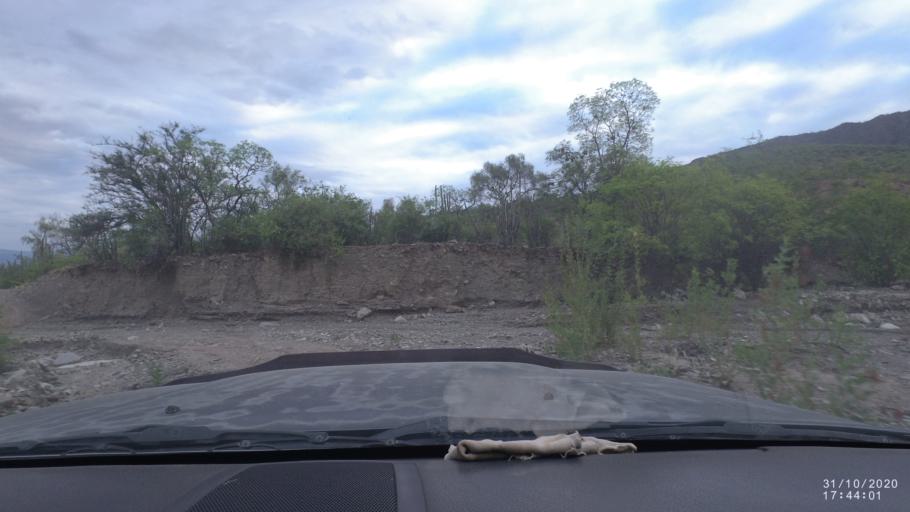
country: BO
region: Chuquisaca
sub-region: Provincia Zudanez
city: Mojocoya
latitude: -18.6101
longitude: -64.5478
